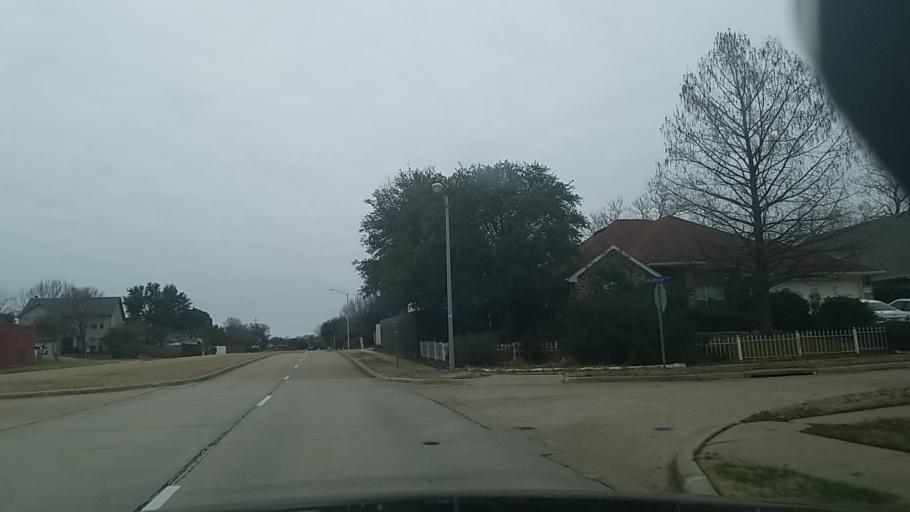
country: US
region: Texas
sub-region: Denton County
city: Corinth
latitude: 33.1361
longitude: -97.0750
